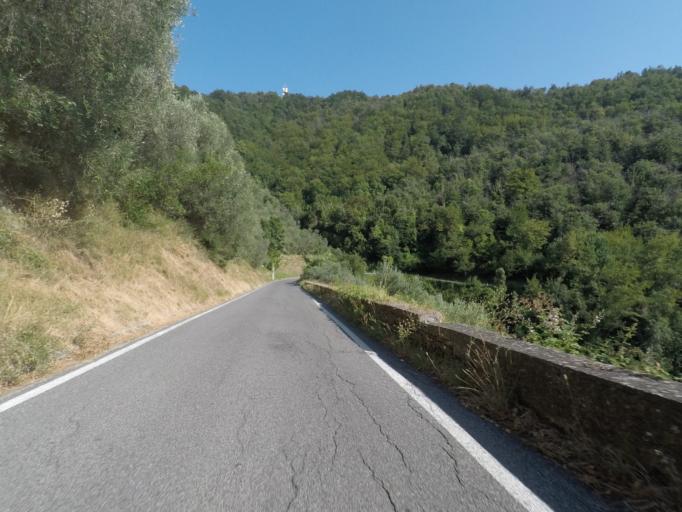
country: IT
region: Liguria
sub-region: Provincia di La Spezia
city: Casano-Dogana-Isola
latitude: 44.0858
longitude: 10.0543
